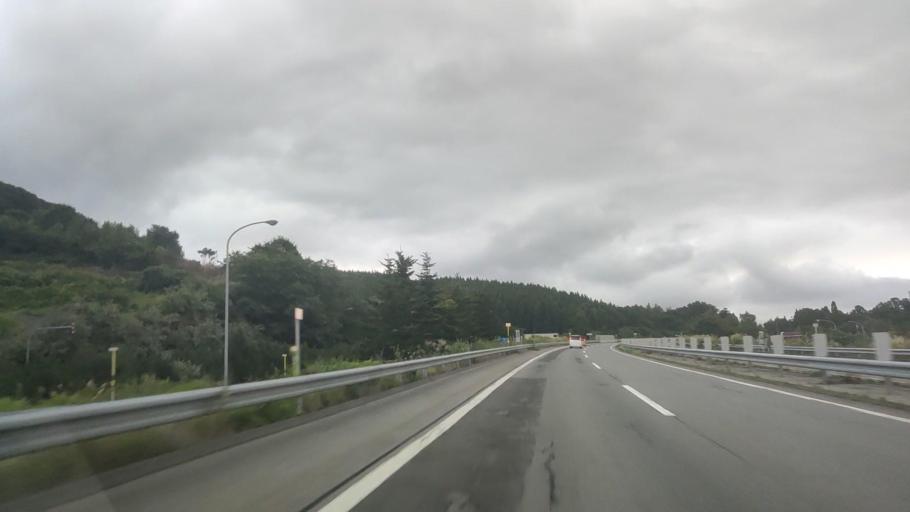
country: JP
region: Hokkaido
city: Nanae
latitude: 41.9002
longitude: 140.7037
